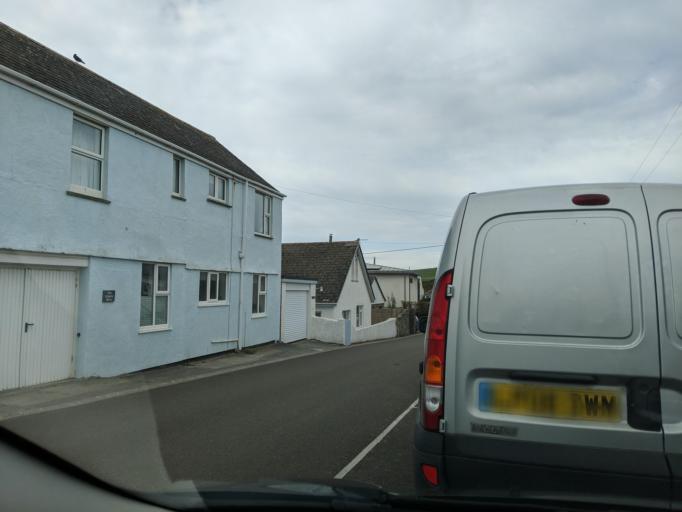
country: GB
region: England
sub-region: Cornwall
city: Polzeath
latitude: 50.5787
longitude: -4.9168
